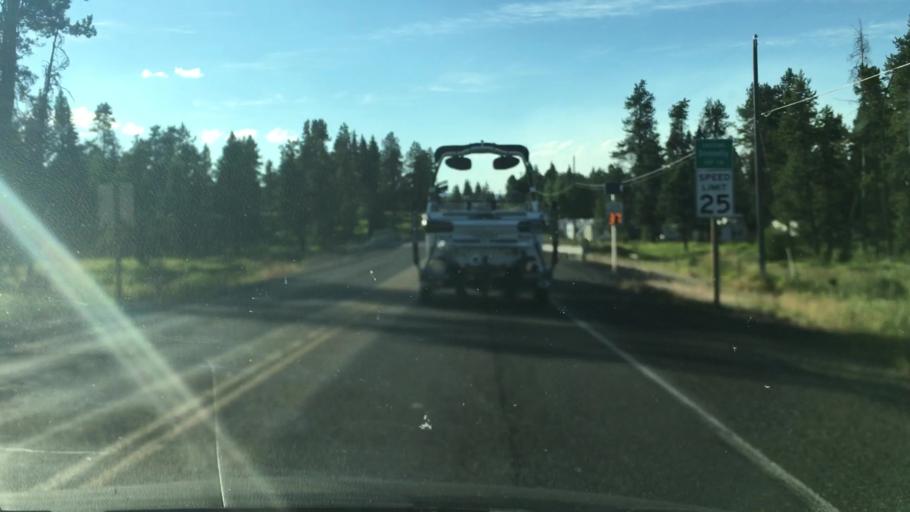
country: US
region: Idaho
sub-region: Valley County
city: McCall
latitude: 44.7264
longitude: -116.0737
